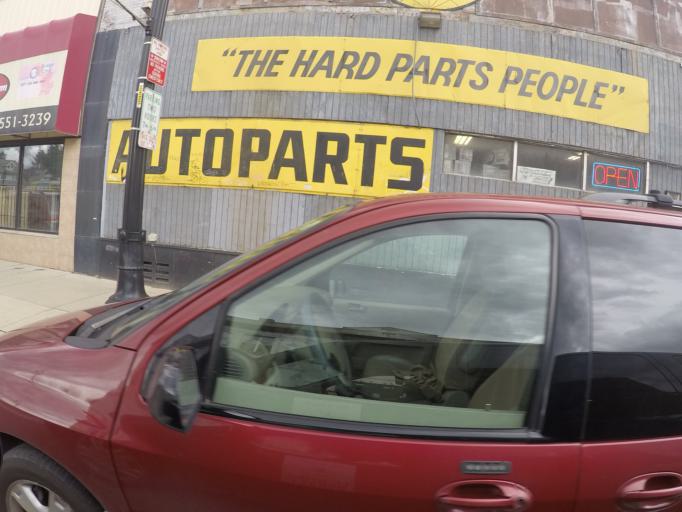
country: US
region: Michigan
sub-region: Wayne County
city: River Rouge
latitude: 42.3118
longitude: -83.1262
